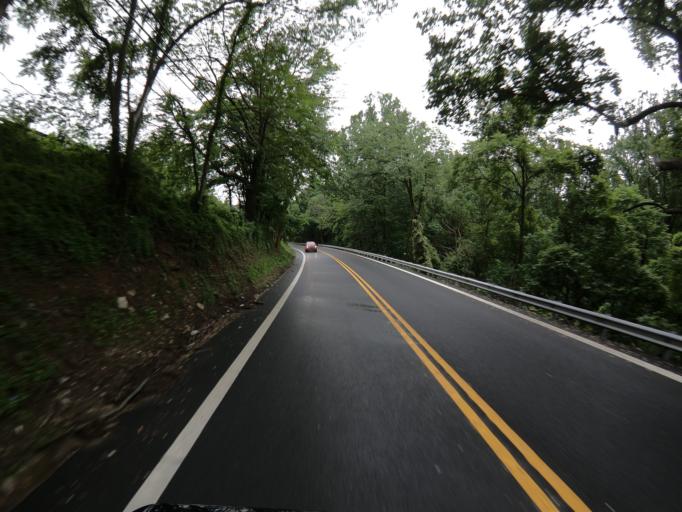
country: US
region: Maryland
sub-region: Washington County
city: Boonsboro
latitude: 39.4804
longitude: -77.6153
